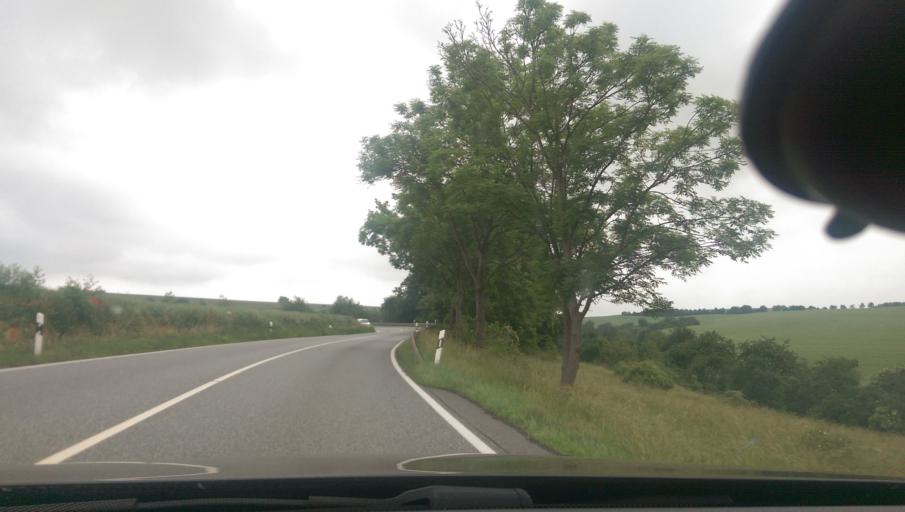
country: DE
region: Thuringia
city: Kleinfurra
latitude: 51.4538
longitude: 10.7913
